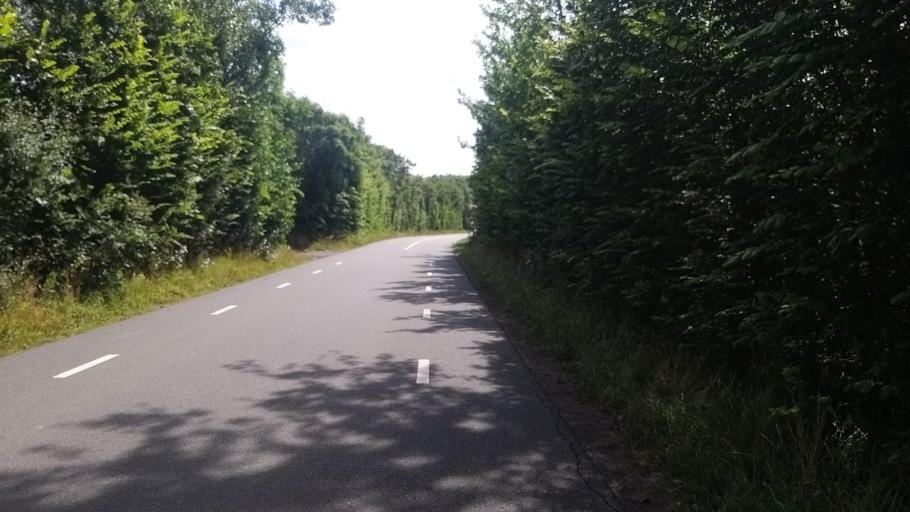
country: NL
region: North Holland
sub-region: Gemeente Texel
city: Den Burg
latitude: 53.0869
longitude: 4.7842
